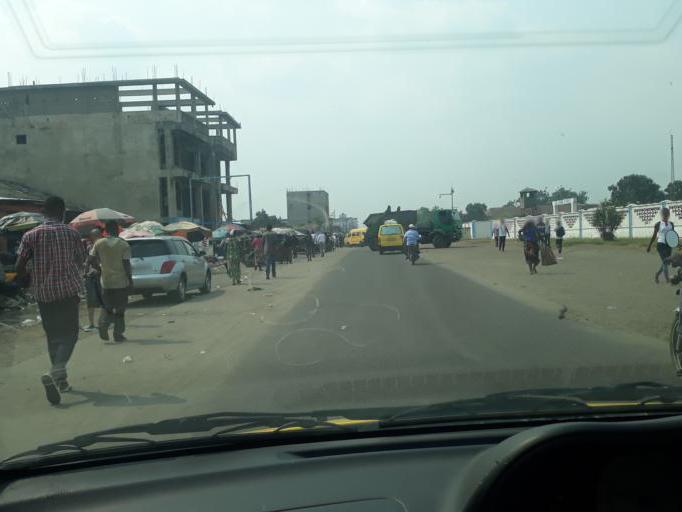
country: CD
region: Kinshasa
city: Kinshasa
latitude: -4.3284
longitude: 15.3197
